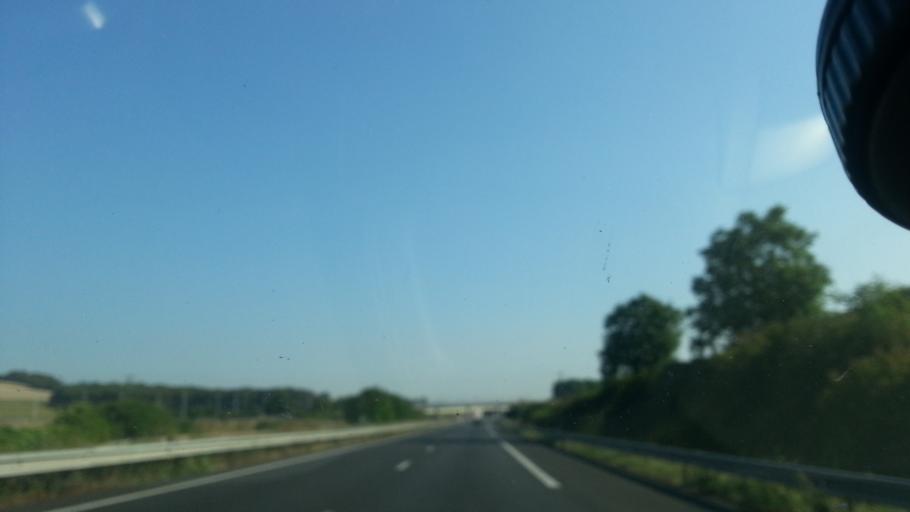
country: FR
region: Poitou-Charentes
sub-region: Departement de la Vienne
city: Les Ormes
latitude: 46.9967
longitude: 0.5513
